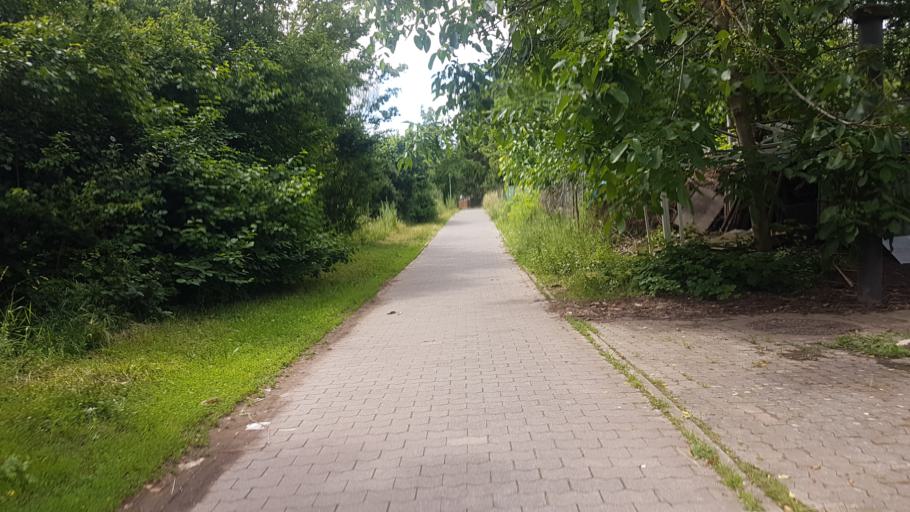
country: DE
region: Saarland
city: Volklingen
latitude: 49.2508
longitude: 6.8391
